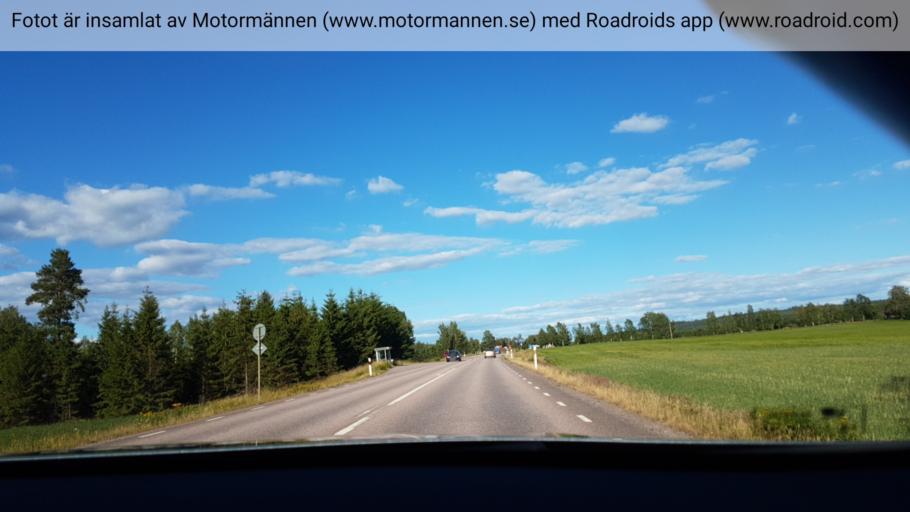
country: SE
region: Vaestra Goetaland
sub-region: Tibro Kommun
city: Tibro
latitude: 58.4538
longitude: 14.2123
